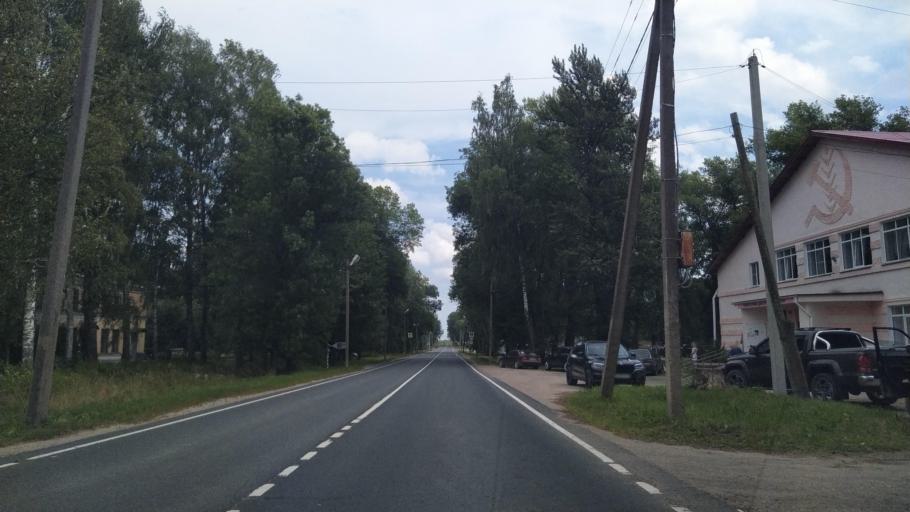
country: RU
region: Pskov
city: Pskov
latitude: 57.7618
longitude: 28.7578
